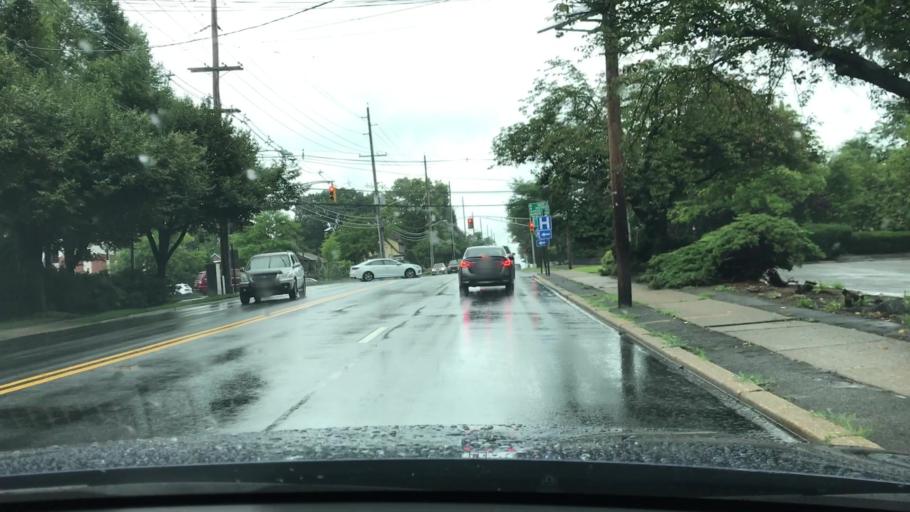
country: US
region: New Jersey
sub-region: Bergen County
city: Oradell
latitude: 40.9616
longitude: -74.0592
